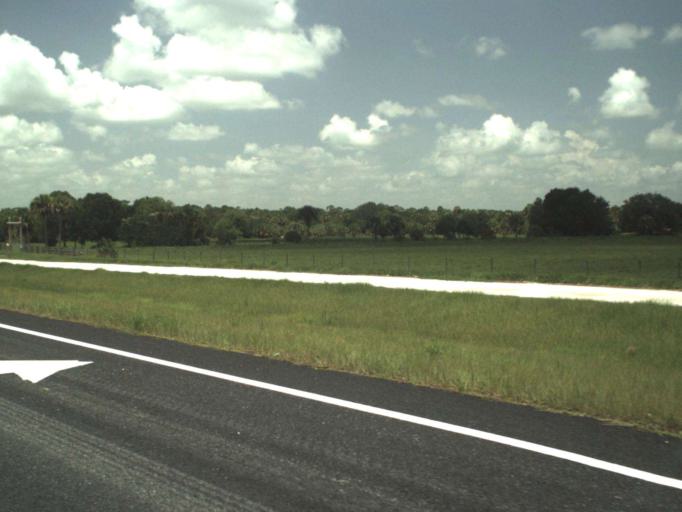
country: US
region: Florida
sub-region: Okeechobee County
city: Taylor Creek
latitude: 27.3399
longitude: -80.6450
